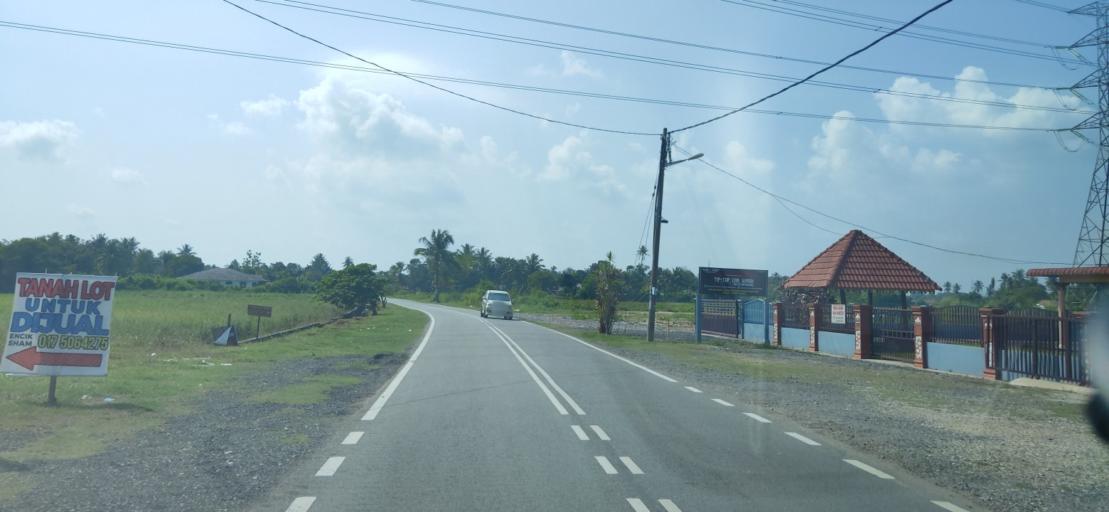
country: MY
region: Kedah
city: Sungai Petani
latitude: 5.6596
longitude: 100.4708
